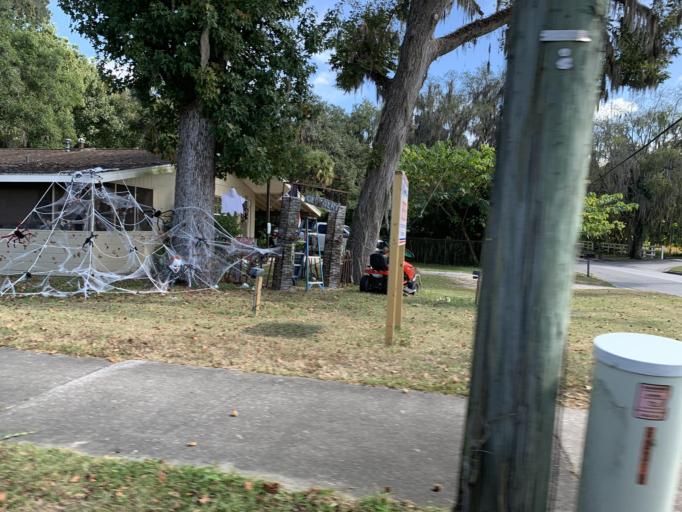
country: US
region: Florida
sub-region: Marion County
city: Ocala
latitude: 29.1769
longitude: -82.1342
